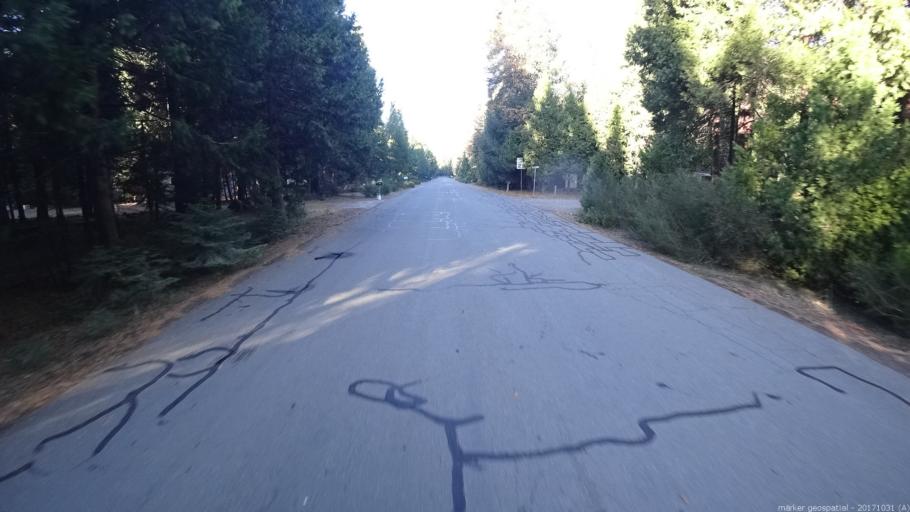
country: US
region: California
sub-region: Shasta County
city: Shingletown
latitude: 40.5248
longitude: -121.7962
